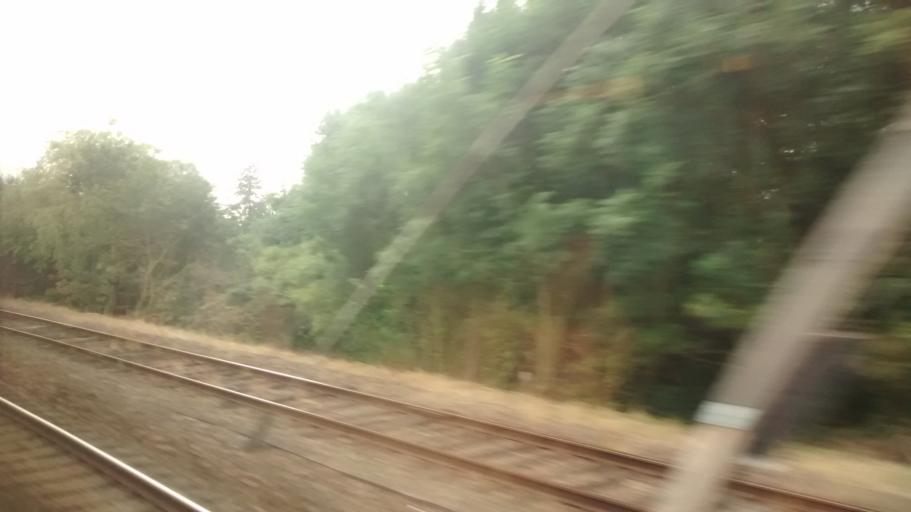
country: FR
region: Pays de la Loire
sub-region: Departement de la Mayenne
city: Sainte-Suzanne
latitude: 48.1340
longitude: -0.2864
